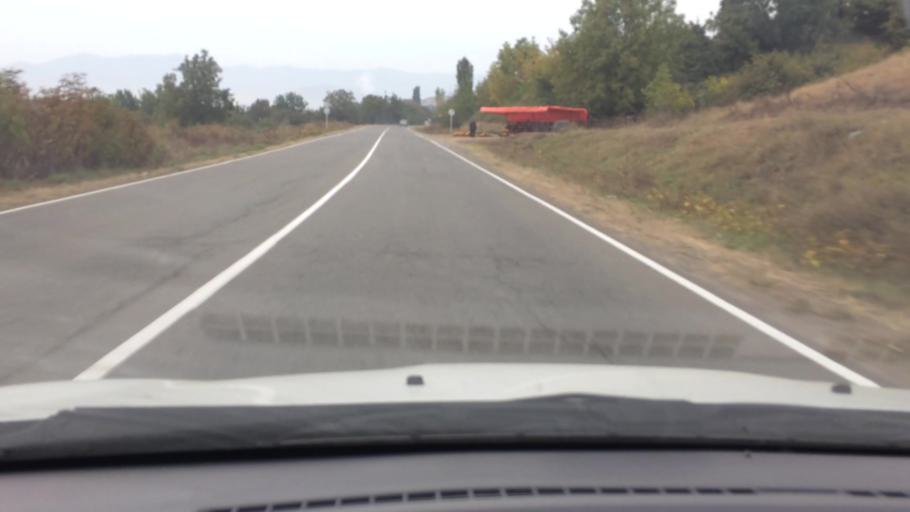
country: GE
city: Naghvarevi
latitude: 41.3036
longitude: 44.7897
